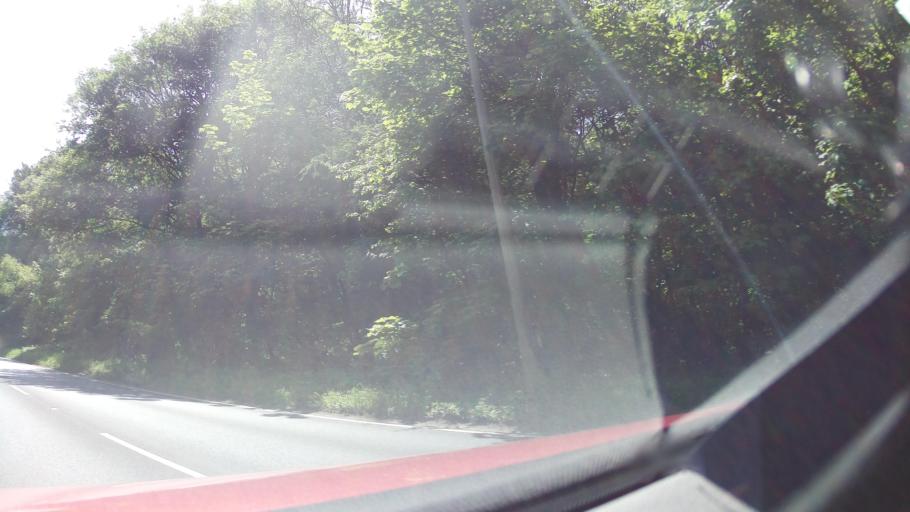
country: GB
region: England
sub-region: North Lincolnshire
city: Broughton
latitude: 53.5507
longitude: -0.5660
